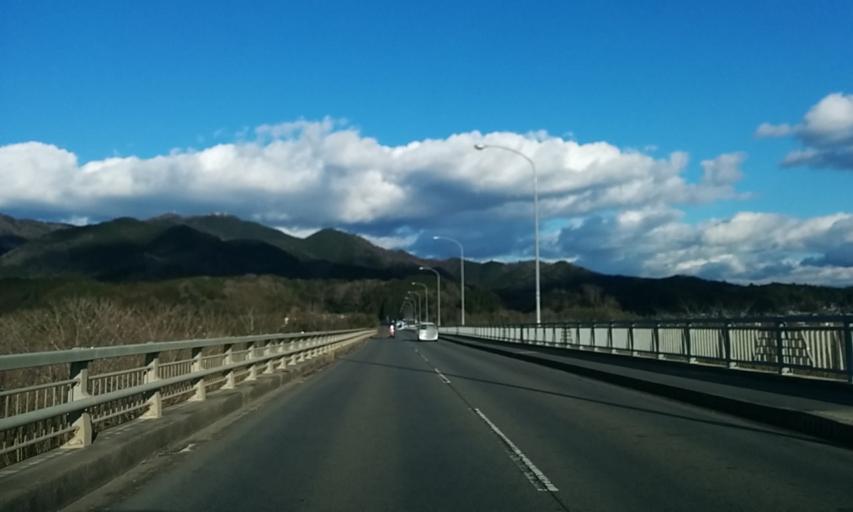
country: JP
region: Kyoto
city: Fukuchiyama
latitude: 35.3147
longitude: 135.1169
